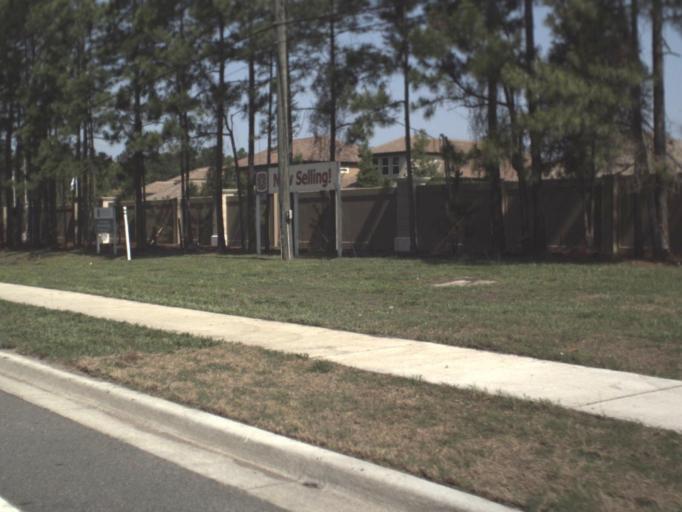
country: US
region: Florida
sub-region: Duval County
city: Jacksonville Beach
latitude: 30.2876
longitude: -81.4743
